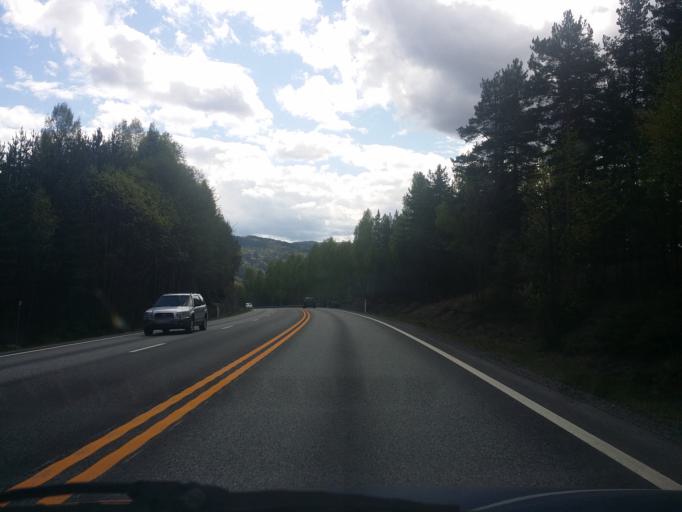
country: NO
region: Buskerud
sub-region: Modum
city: Vikersund
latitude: 59.9376
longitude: 9.9616
